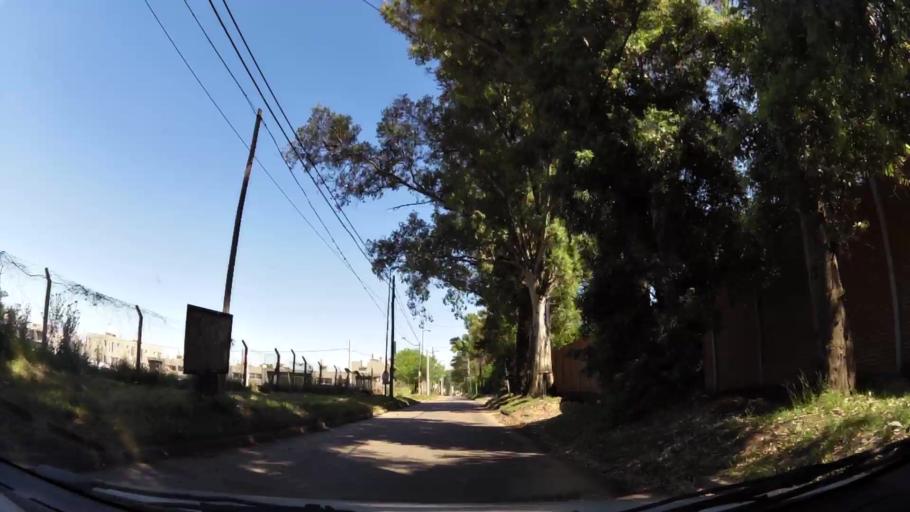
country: AR
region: Buenos Aires
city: Ituzaingo
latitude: -34.6236
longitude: -58.6620
